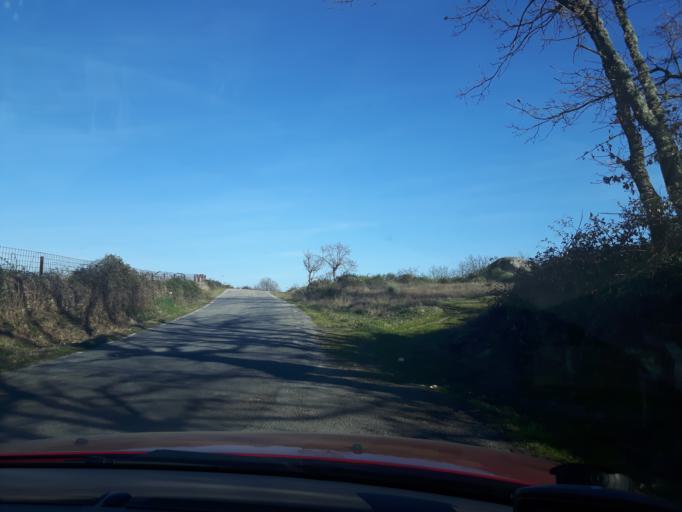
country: ES
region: Castille and Leon
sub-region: Provincia de Salamanca
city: Saldeana
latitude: 41.0172
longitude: -6.6352
